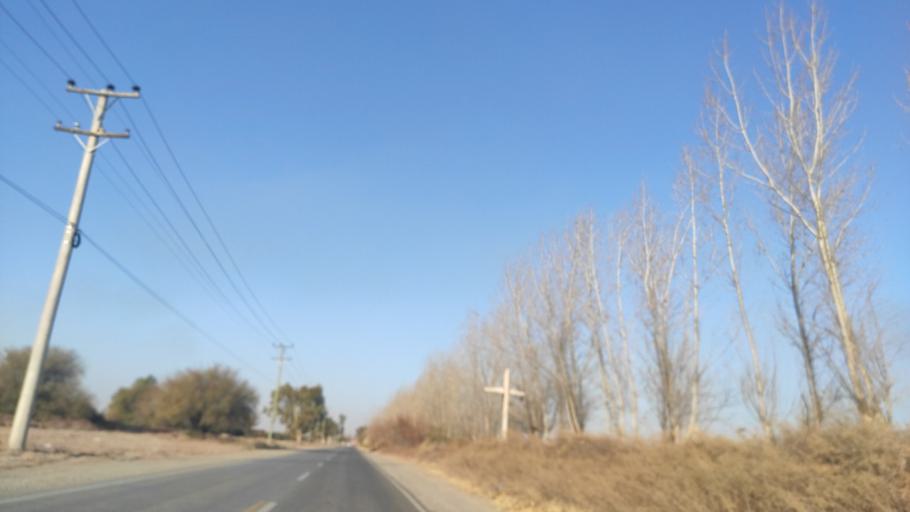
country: AR
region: San Juan
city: Villa Media Agua
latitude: -31.9792
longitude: -68.4508
